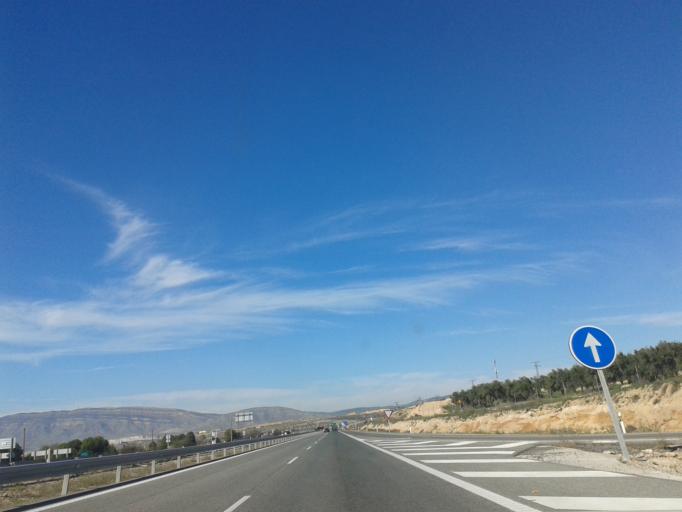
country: ES
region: Castille-La Mancha
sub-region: Provincia de Albacete
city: Caudete
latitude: 38.6970
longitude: -0.9165
